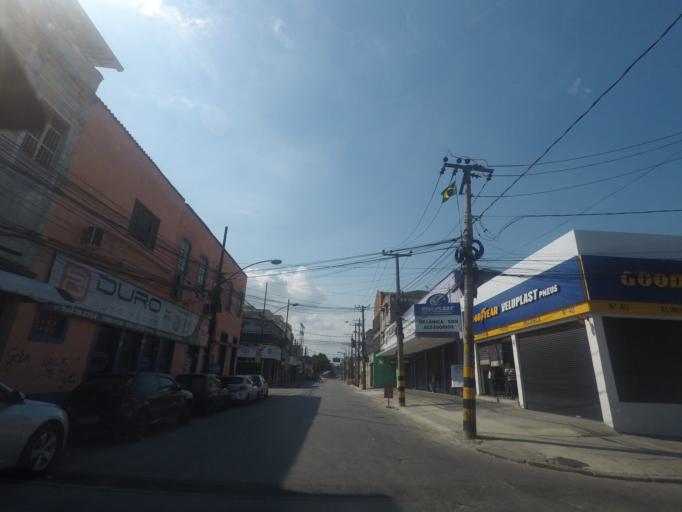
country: BR
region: Rio de Janeiro
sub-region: Rio De Janeiro
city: Rio de Janeiro
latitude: -22.8993
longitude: -43.2168
